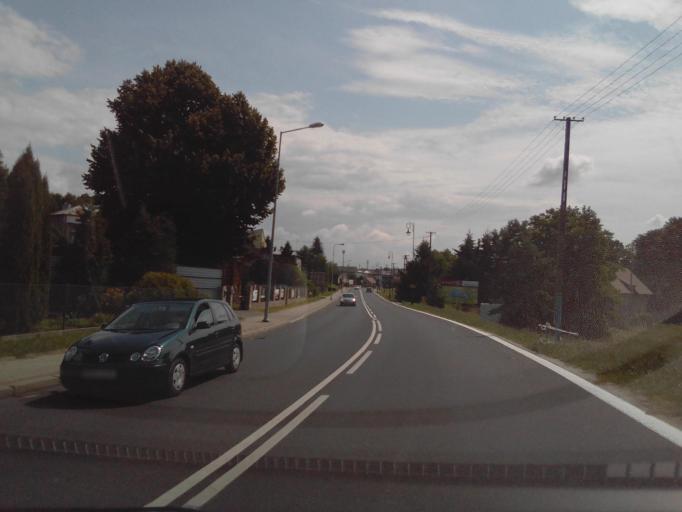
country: PL
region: Subcarpathian Voivodeship
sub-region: Powiat ropczycko-sedziszowski
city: Ropczyce
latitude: 50.0539
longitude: 21.6021
